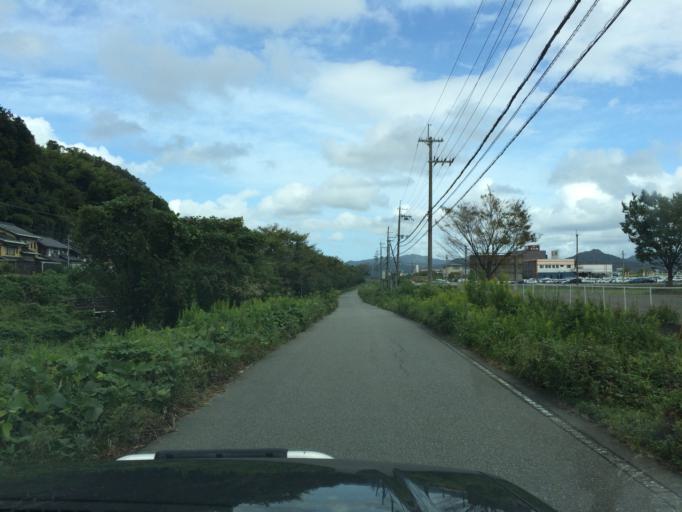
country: JP
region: Hyogo
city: Toyooka
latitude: 35.5044
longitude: 134.8093
